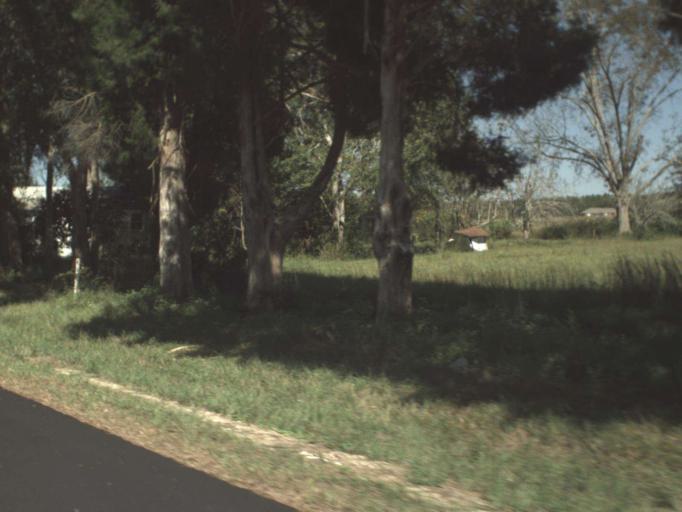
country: US
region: Florida
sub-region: Walton County
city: DeFuniak Springs
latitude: 30.8051
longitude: -86.1970
